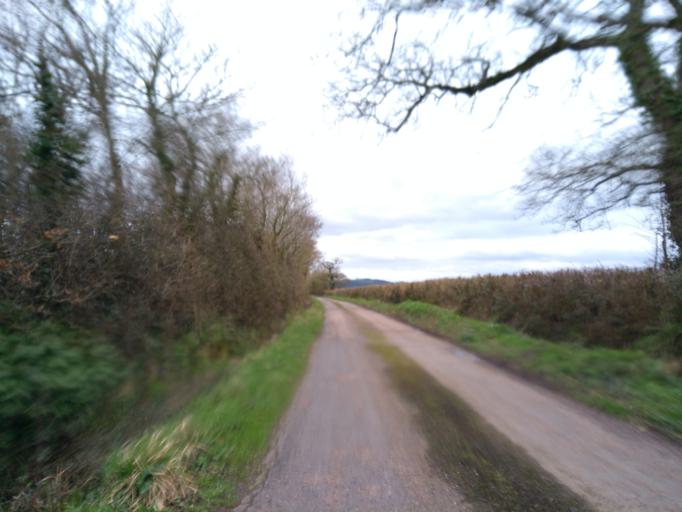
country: GB
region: England
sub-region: Devon
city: Heavitree
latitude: 50.7976
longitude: -3.5000
